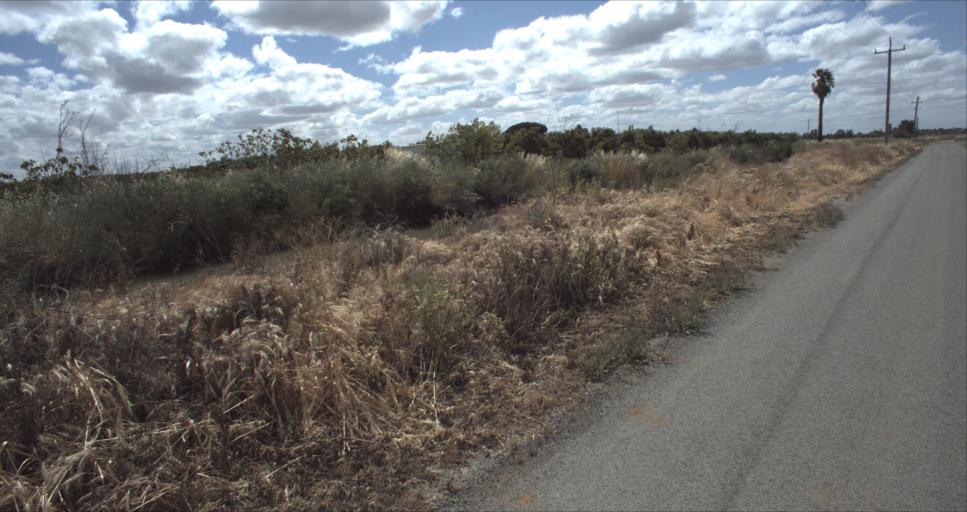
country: AU
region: New South Wales
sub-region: Leeton
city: Leeton
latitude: -34.5817
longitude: 146.3921
